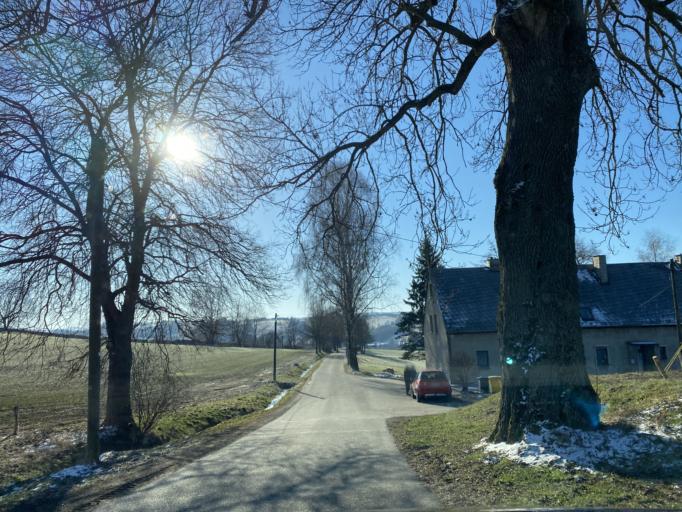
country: DE
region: Saxony
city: Wiesa
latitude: 50.6185
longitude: 13.0059
